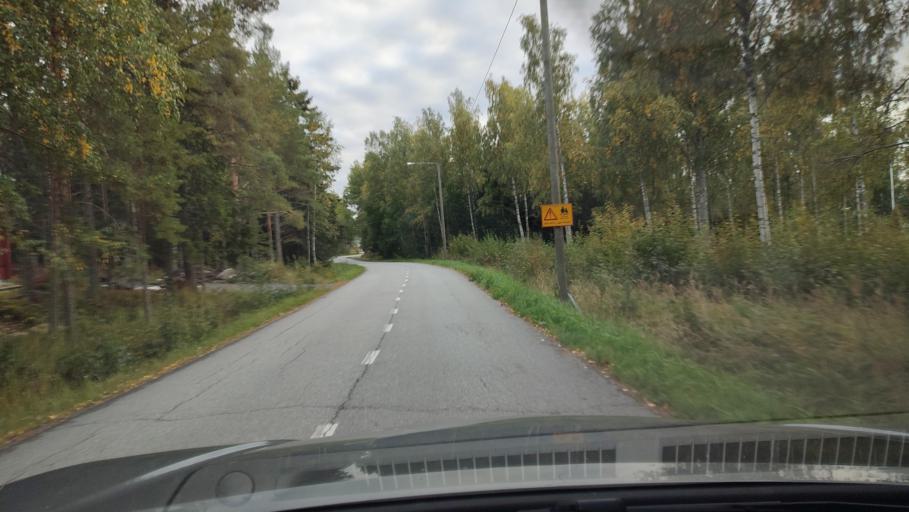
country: FI
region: Ostrobothnia
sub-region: Sydosterbotten
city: Kristinestad
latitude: 62.2588
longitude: 21.3836
